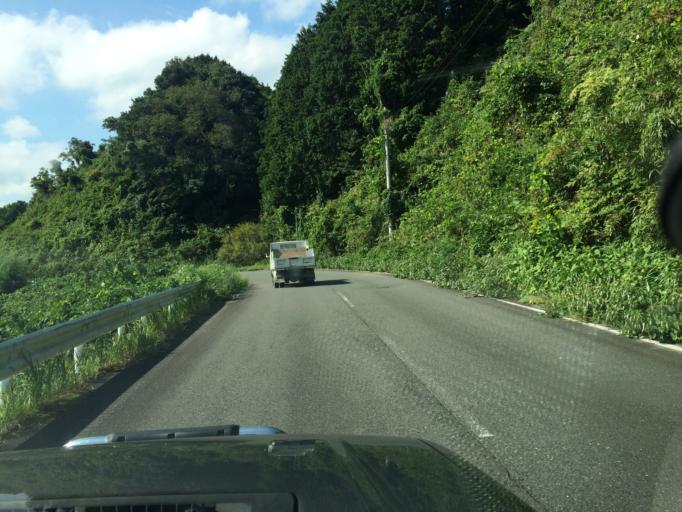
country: JP
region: Mie
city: Nabari
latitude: 34.6991
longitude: 135.9743
